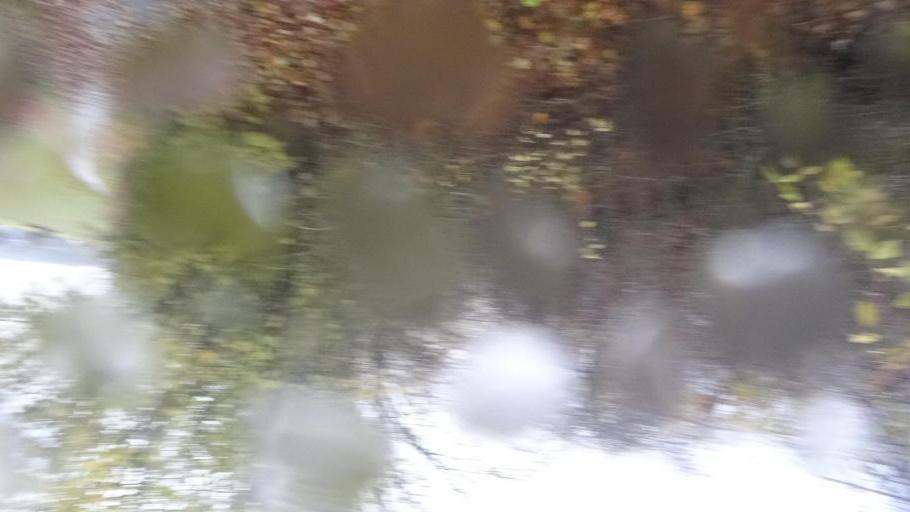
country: DE
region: Rheinland-Pfalz
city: Wiebelsheim
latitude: 50.0753
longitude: 7.6278
